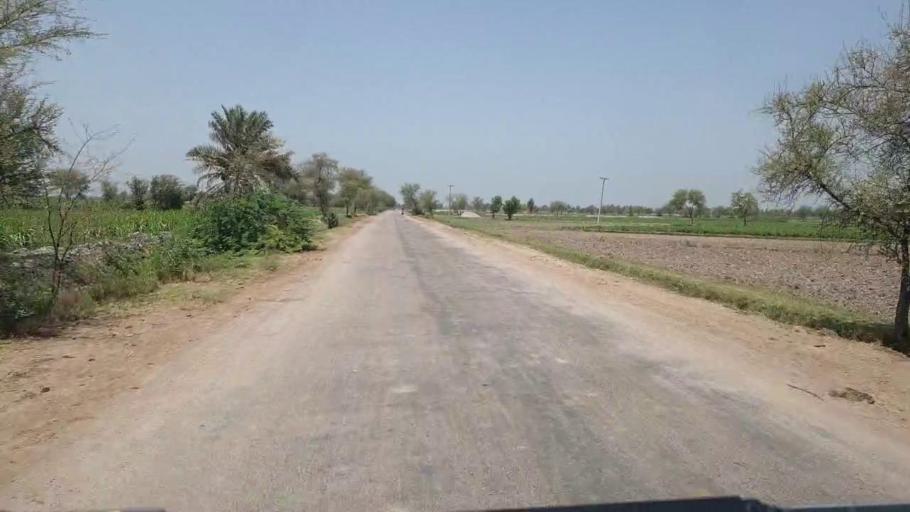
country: PK
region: Sindh
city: Nawabshah
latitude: 26.3489
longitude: 68.3915
